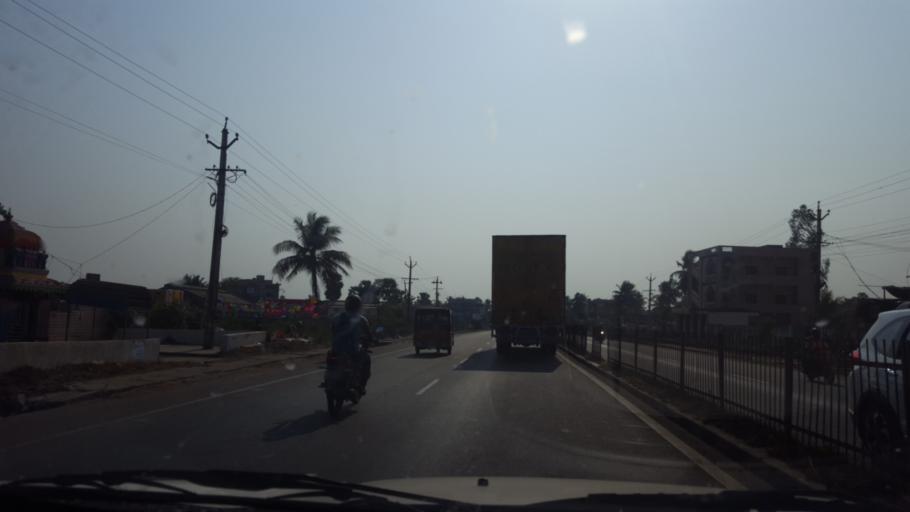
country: IN
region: Andhra Pradesh
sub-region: Vishakhapatnam
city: Anakapalle
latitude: 17.6813
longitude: 82.9818
